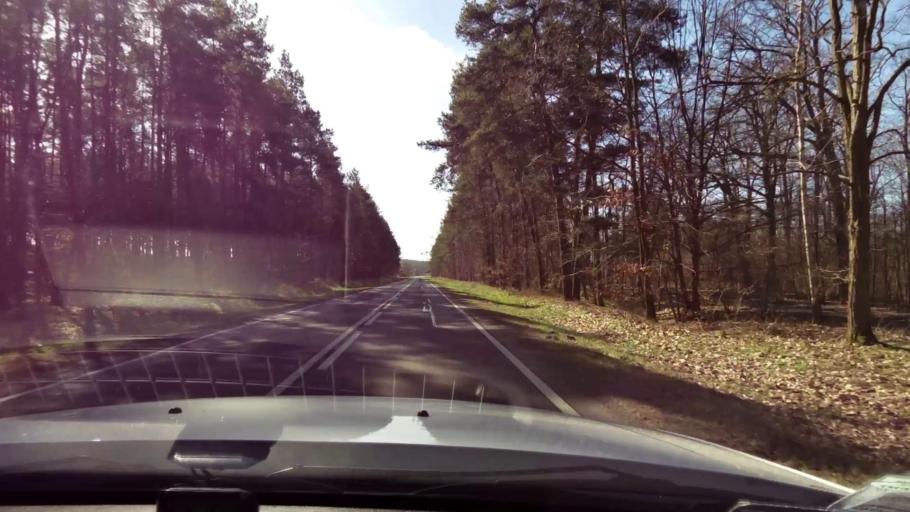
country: PL
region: West Pomeranian Voivodeship
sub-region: Powiat gryfinski
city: Gryfino
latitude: 53.2038
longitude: 14.4815
